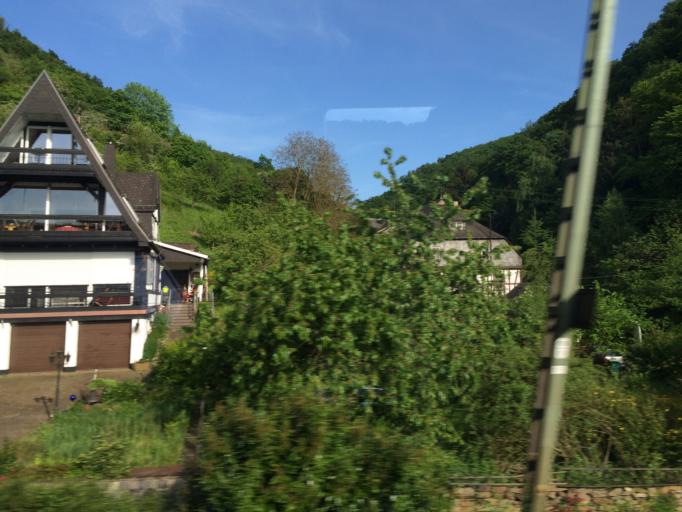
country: DE
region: Rheinland-Pfalz
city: Spay
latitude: 50.2506
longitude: 7.6524
